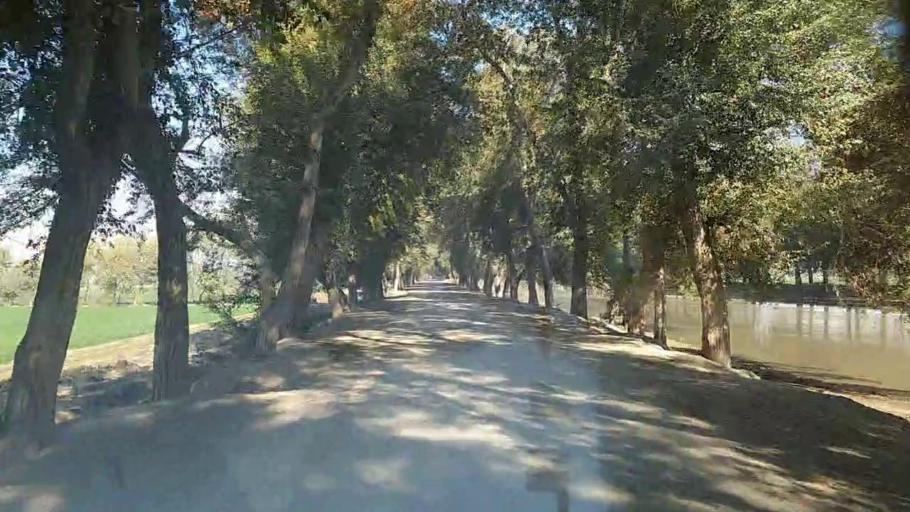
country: PK
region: Sindh
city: Khairpur
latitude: 27.9991
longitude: 69.6523
